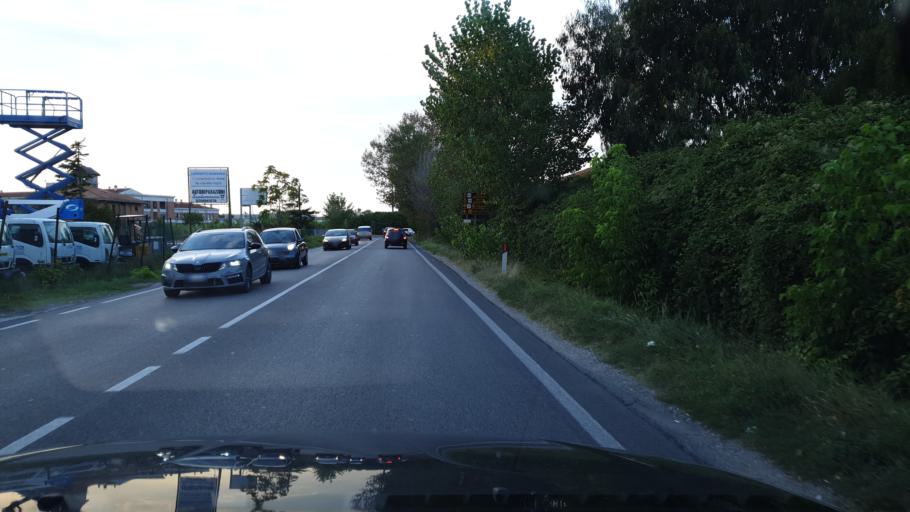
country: IT
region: Emilia-Romagna
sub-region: Provincia di Rimini
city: Rivazzurra
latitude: 44.0361
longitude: 12.5995
